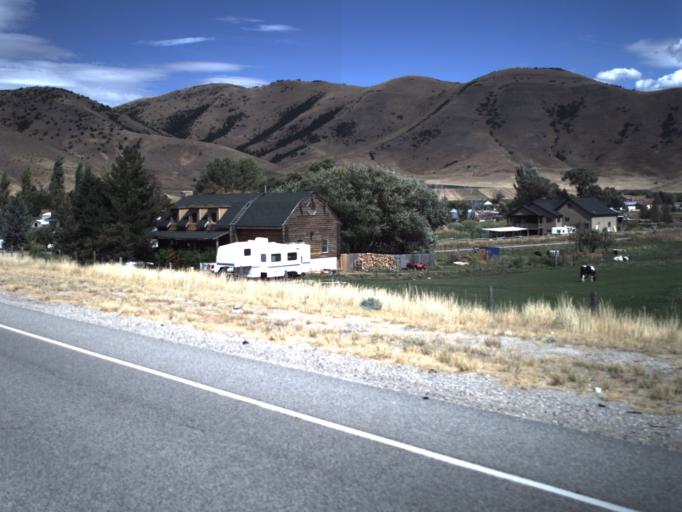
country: US
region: Utah
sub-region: Box Elder County
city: Brigham City
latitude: 41.5084
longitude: -111.9452
